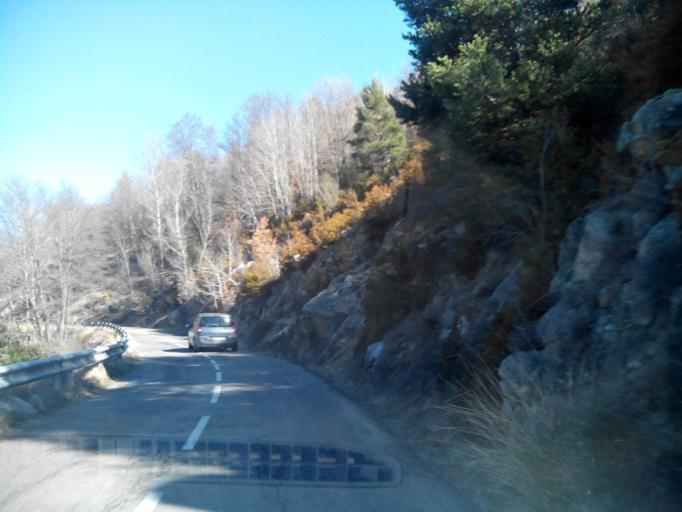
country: ES
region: Catalonia
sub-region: Provincia de Lleida
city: Lles de Cerdanya
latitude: 42.3638
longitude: 1.6854
